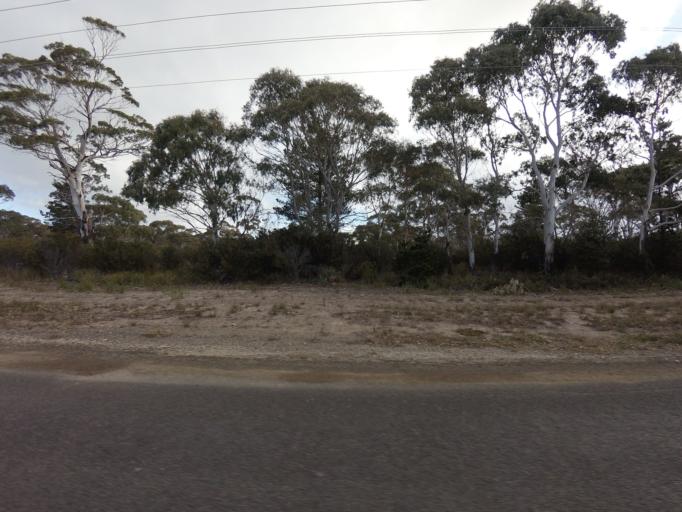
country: AU
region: Tasmania
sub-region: Break O'Day
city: St Helens
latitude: -42.0970
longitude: 148.0863
